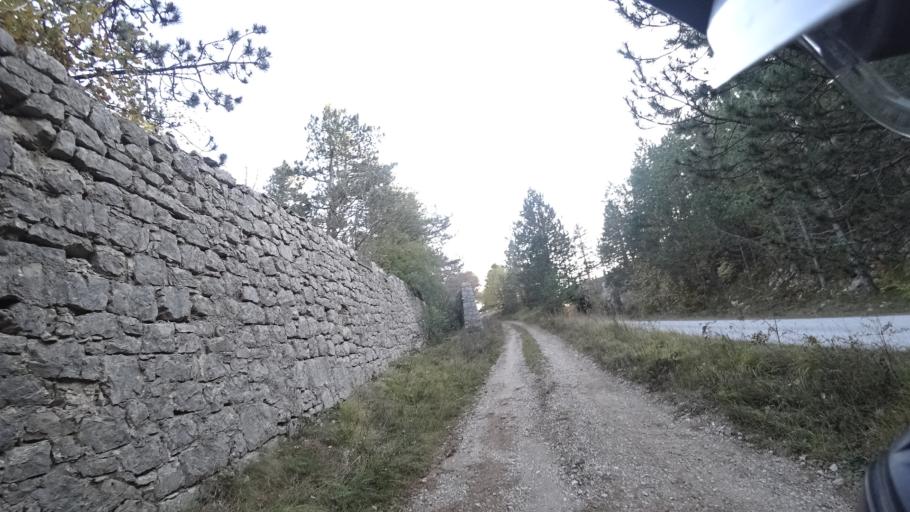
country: HR
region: Primorsko-Goranska
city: Klana
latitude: 45.4975
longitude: 14.4079
